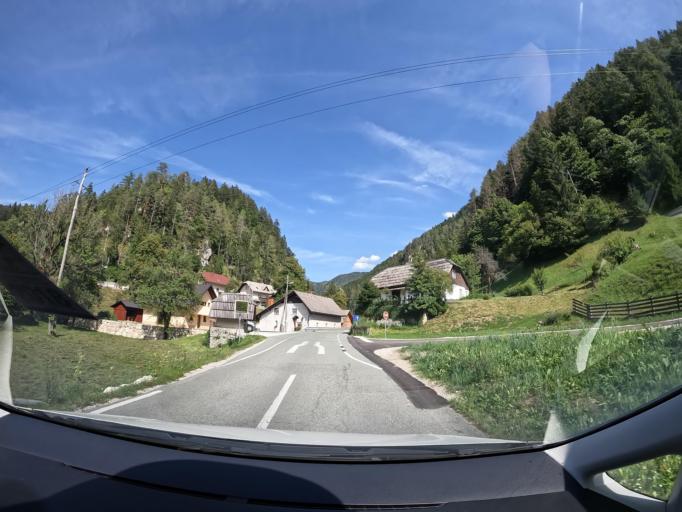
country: SI
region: Jesenice
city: Koroska Bela
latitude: 46.4554
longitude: 14.0997
